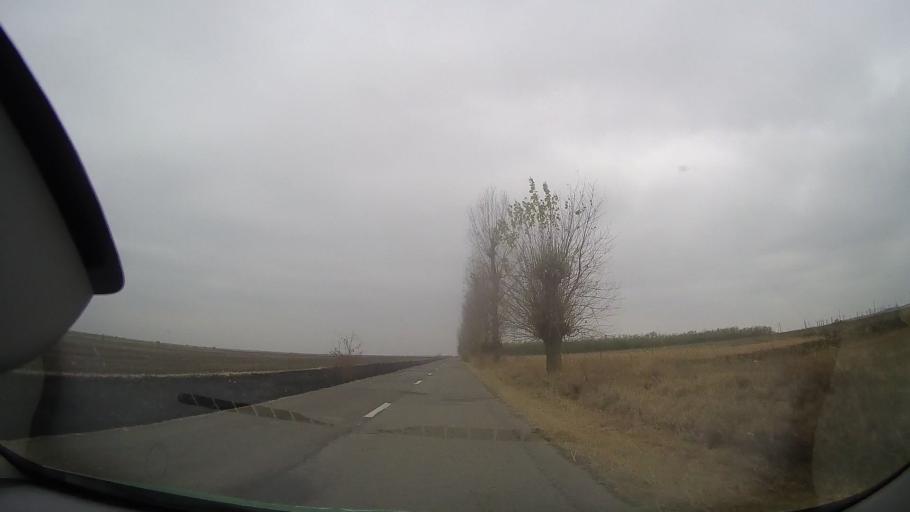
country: RO
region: Ialomita
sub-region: Comuna Valea Macrisului
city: Valea Macrisului
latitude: 44.7419
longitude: 26.8647
